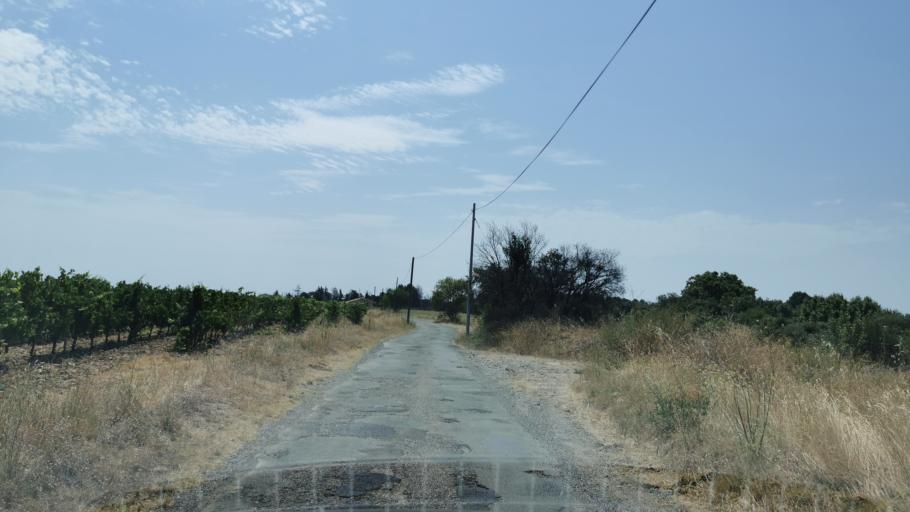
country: FR
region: Languedoc-Roussillon
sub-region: Departement de l'Aude
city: Bize-Minervois
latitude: 43.2977
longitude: 2.8772
